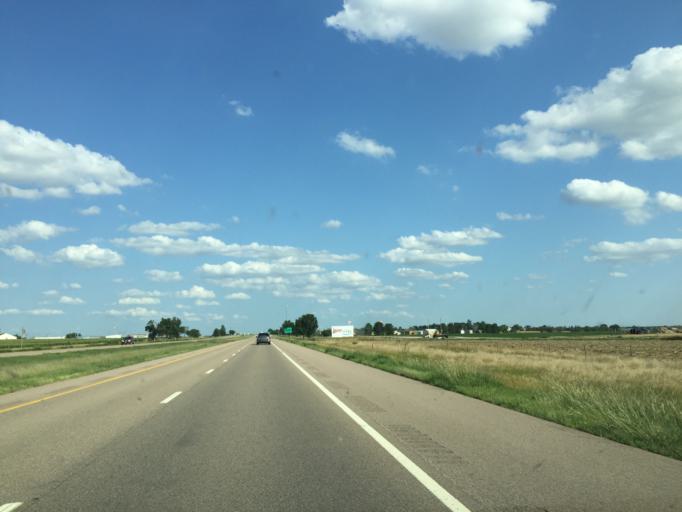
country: US
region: Kansas
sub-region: Gove County
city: Gove
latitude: 39.0616
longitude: -100.2497
